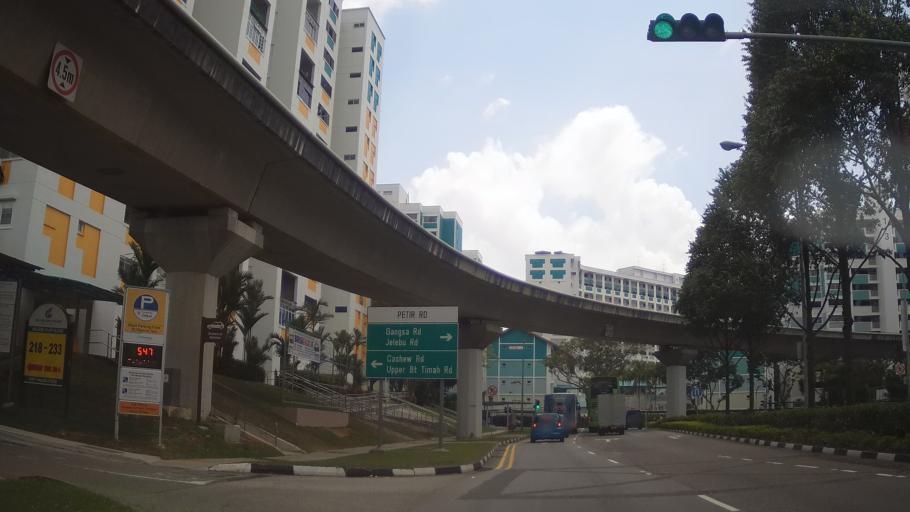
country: MY
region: Johor
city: Johor Bahru
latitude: 1.3760
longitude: 103.7711
